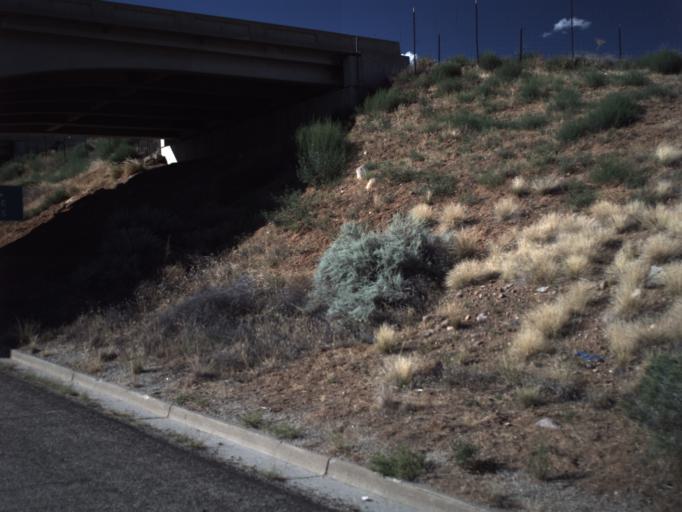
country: US
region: Utah
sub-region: Washington County
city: Toquerville
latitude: 37.2835
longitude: -113.3060
